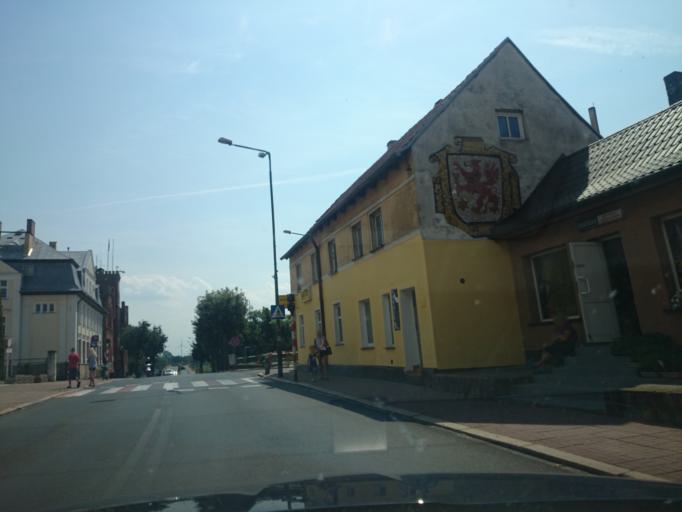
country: PL
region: West Pomeranian Voivodeship
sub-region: Powiat kamienski
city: Wolin
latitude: 53.8446
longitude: 14.6152
